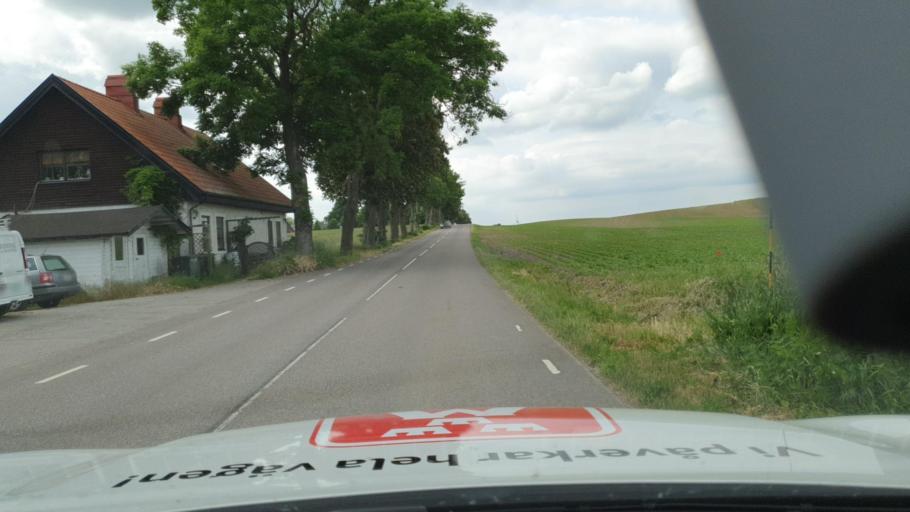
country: SE
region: Skane
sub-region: Svedala Kommun
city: Klagerup
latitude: 55.5860
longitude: 13.2800
